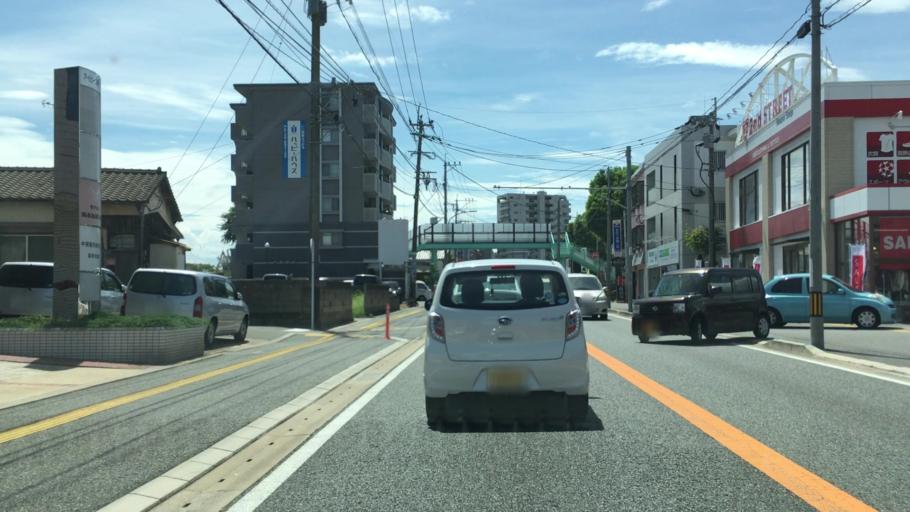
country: JP
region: Fukuoka
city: Onojo
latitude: 33.5430
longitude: 130.4721
